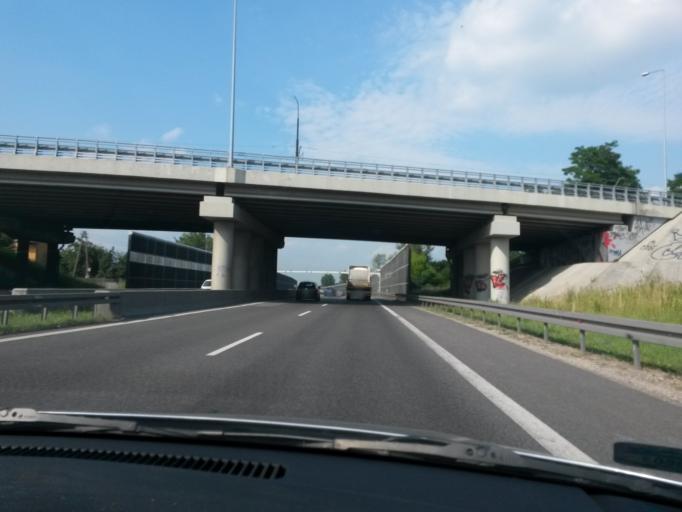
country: PL
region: Silesian Voivodeship
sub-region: Dabrowa Gornicza
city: Dabrowa Gornicza
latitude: 50.2732
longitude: 19.2070
